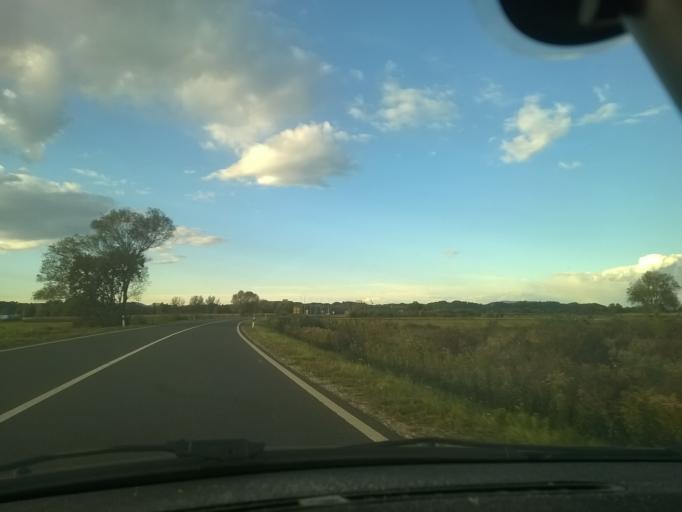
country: HR
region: Zagrebacka
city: Pojatno
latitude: 45.9302
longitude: 15.8199
